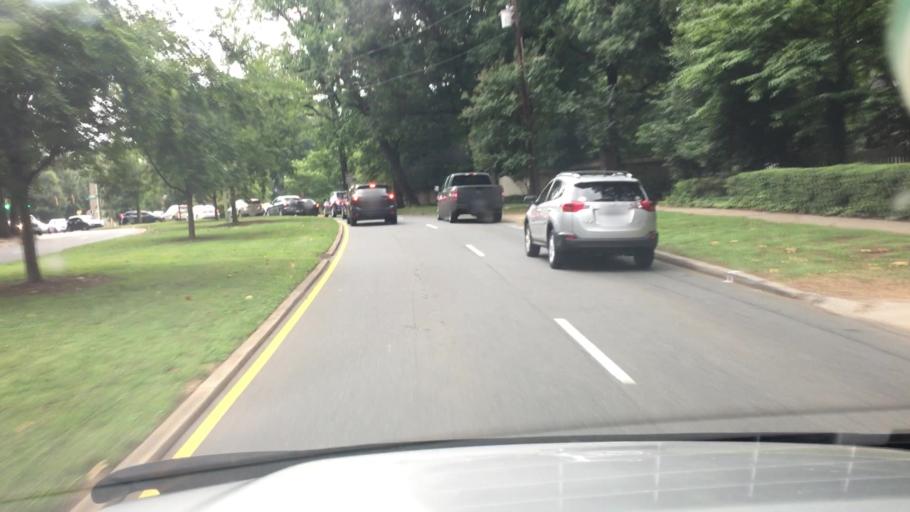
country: US
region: North Carolina
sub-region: Mecklenburg County
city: Charlotte
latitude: 35.1969
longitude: -80.8284
